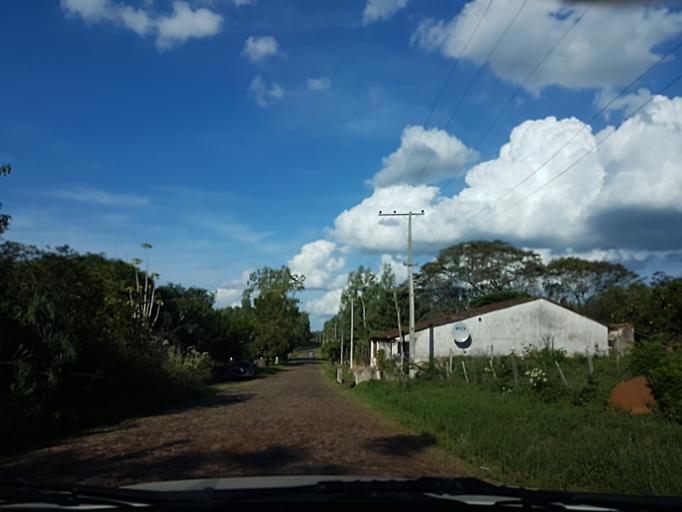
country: PY
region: Cordillera
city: Arroyos y Esteros
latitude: -24.9967
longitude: -57.1530
